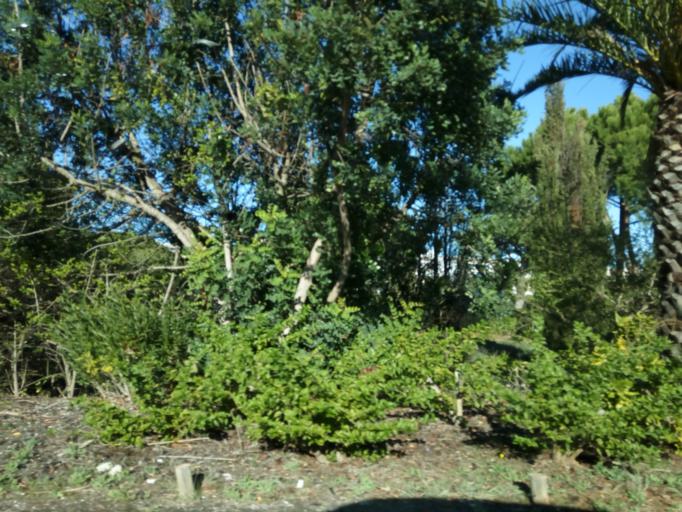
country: PT
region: Faro
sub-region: Loule
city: Vilamoura
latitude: 37.0894
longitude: -8.1214
